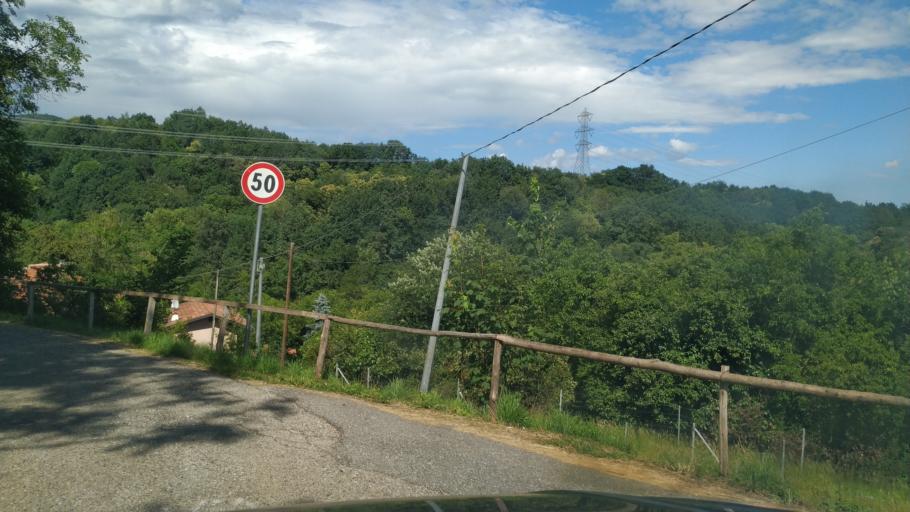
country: IT
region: Piedmont
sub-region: Provincia di Torino
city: Baldissero Canavese
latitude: 45.4113
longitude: 7.7176
